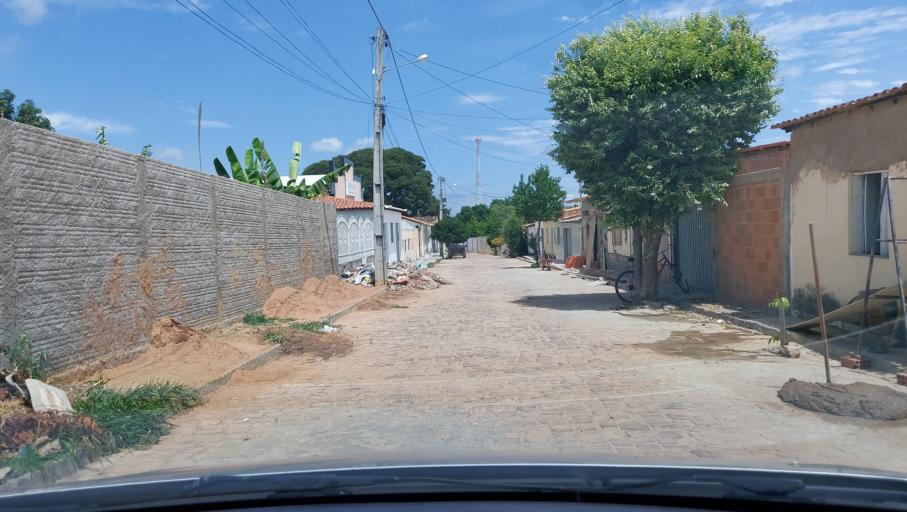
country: BR
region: Bahia
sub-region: Oliveira Dos Brejinhos
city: Beira Rio
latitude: -11.9976
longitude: -42.6293
